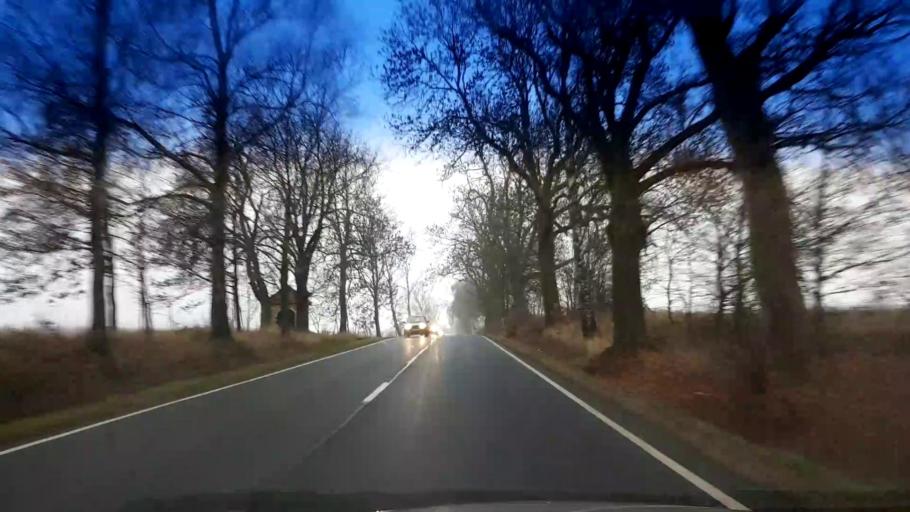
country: CZ
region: Karlovarsky
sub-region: Okres Cheb
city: Cheb
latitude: 50.0564
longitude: 12.3571
